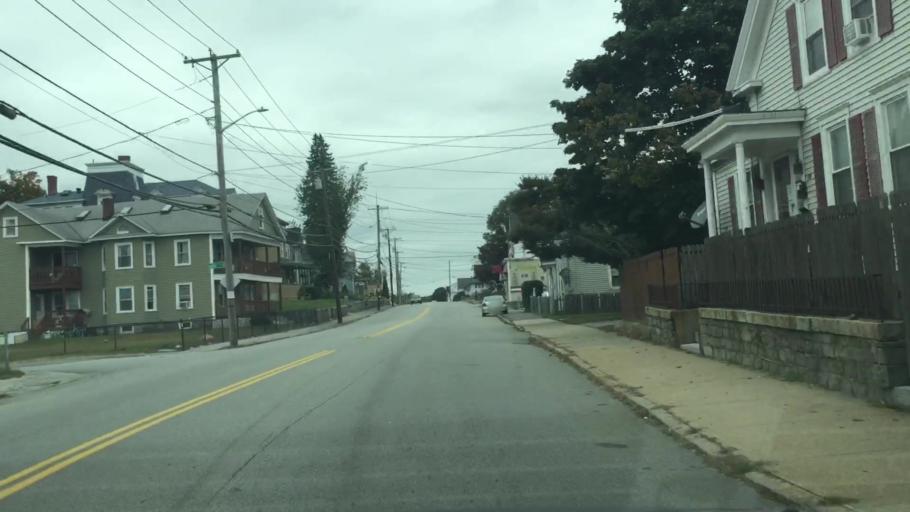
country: US
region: Massachusetts
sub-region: Middlesex County
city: Lowell
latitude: 42.6519
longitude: -71.3345
